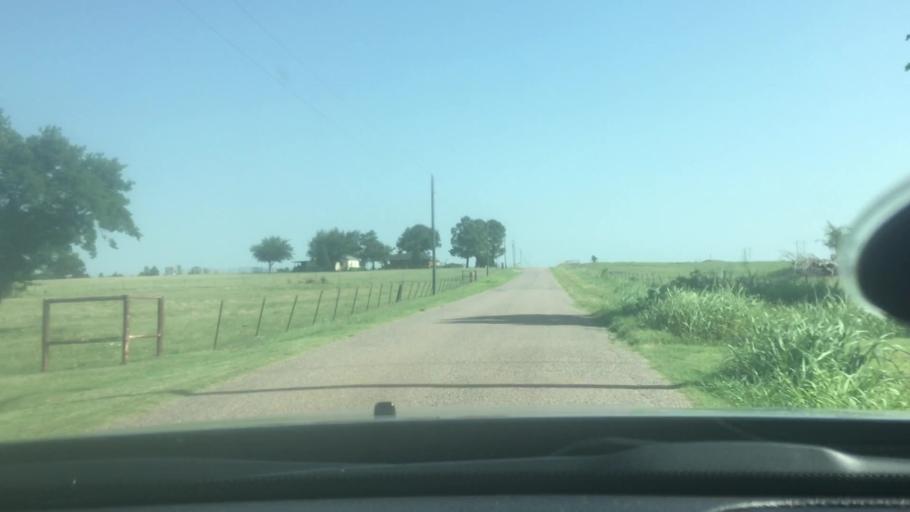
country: US
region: Oklahoma
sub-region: Bryan County
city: Calera
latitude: 33.9471
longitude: -96.4613
